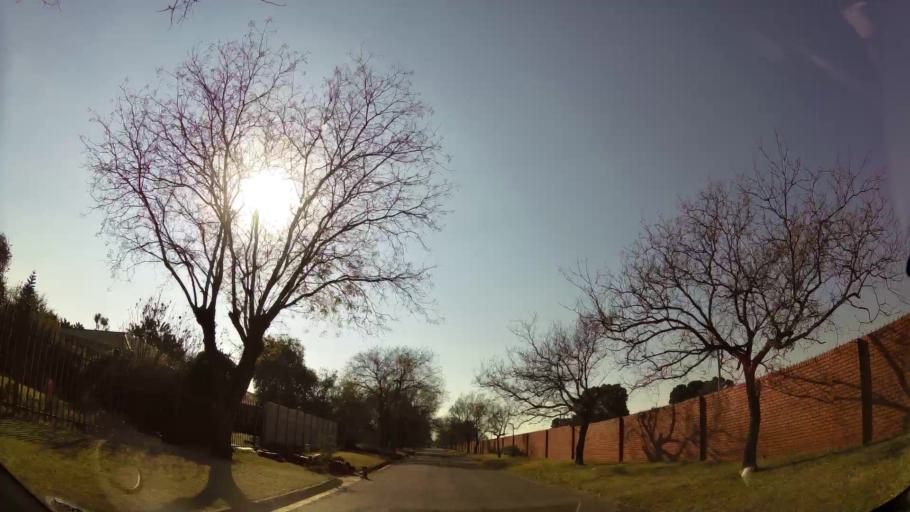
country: ZA
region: Gauteng
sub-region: Ekurhuleni Metropolitan Municipality
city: Benoni
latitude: -26.1575
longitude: 28.3067
